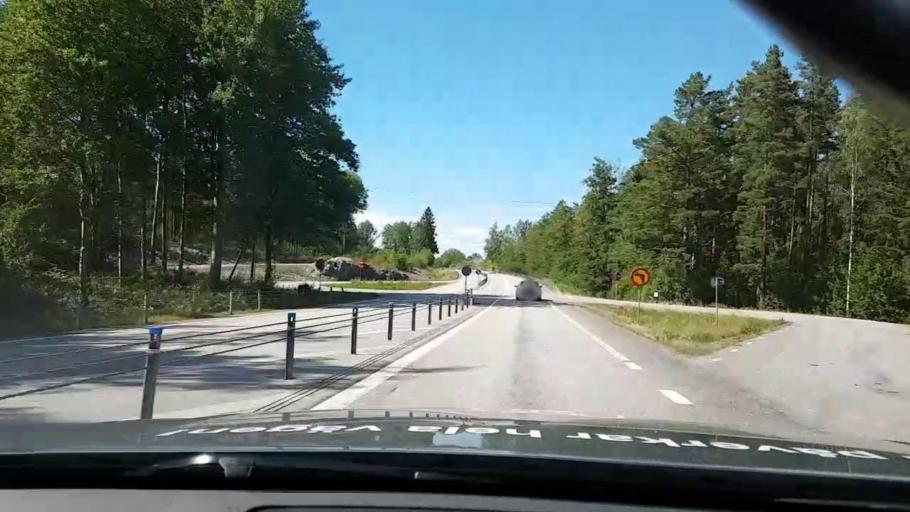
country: SE
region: Kalmar
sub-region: Vasterviks Kommun
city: Gamleby
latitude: 57.8601
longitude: 16.4273
